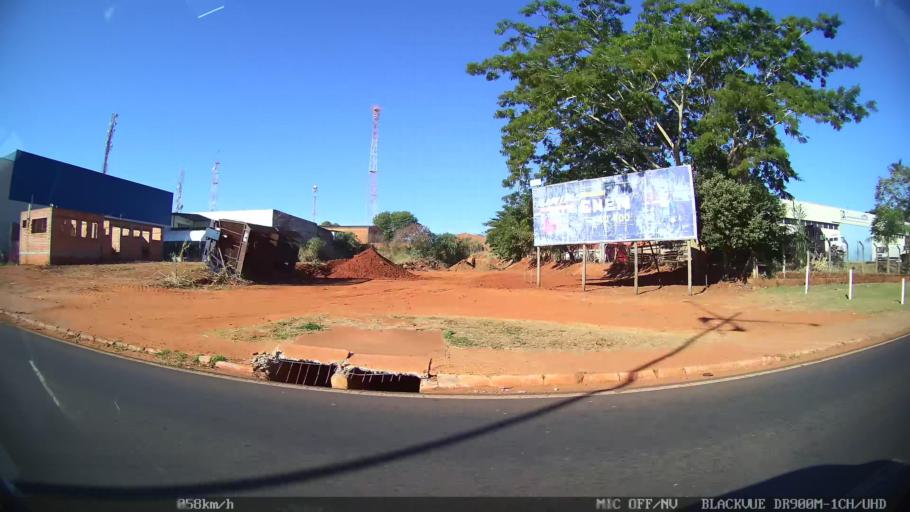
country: BR
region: Sao Paulo
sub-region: Olimpia
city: Olimpia
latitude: -20.7299
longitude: -48.9049
